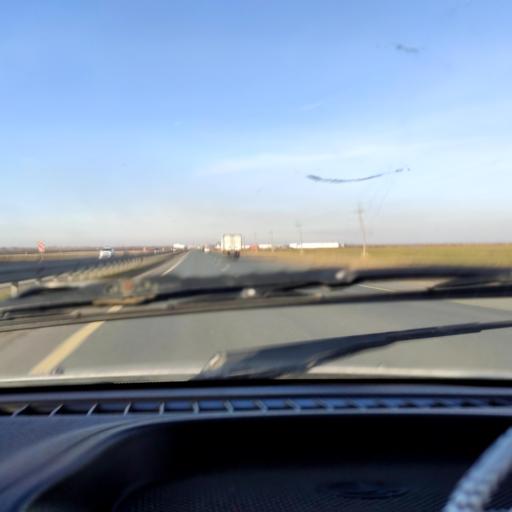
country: RU
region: Samara
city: Zhigulevsk
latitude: 53.5491
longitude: 49.5087
